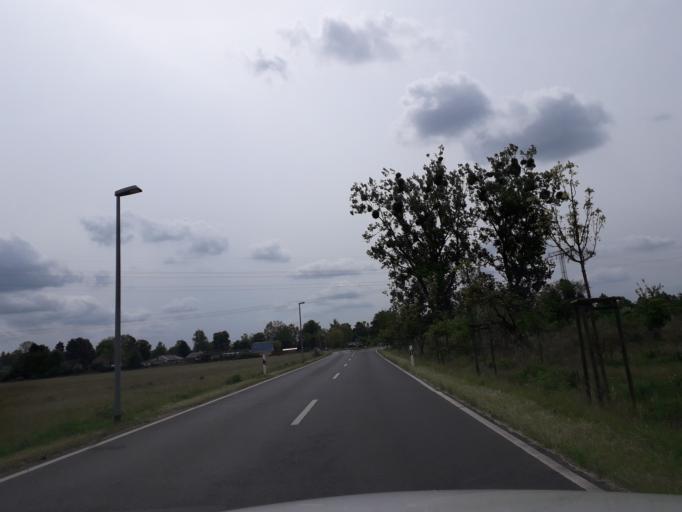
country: DE
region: Brandenburg
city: Brieselang
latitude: 52.6075
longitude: 12.9888
